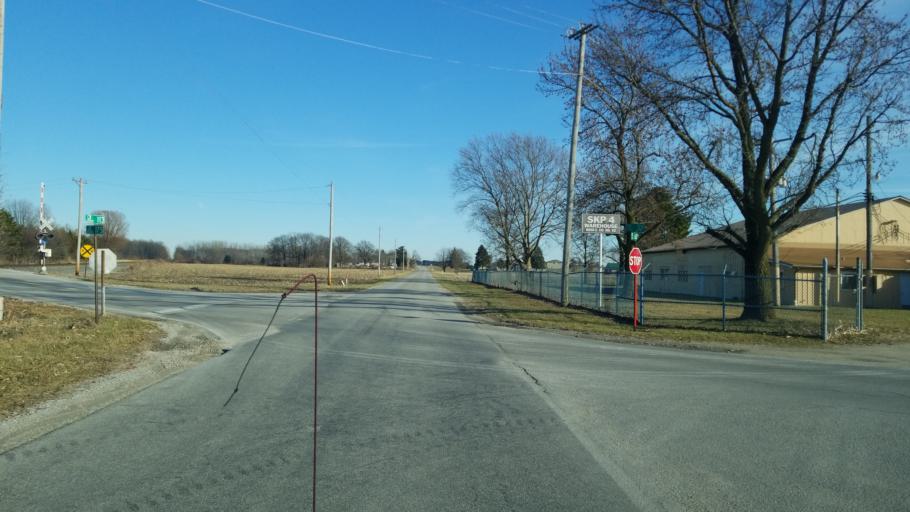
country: US
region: Ohio
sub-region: Sandusky County
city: Green Springs
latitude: 41.2559
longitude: -83.0125
